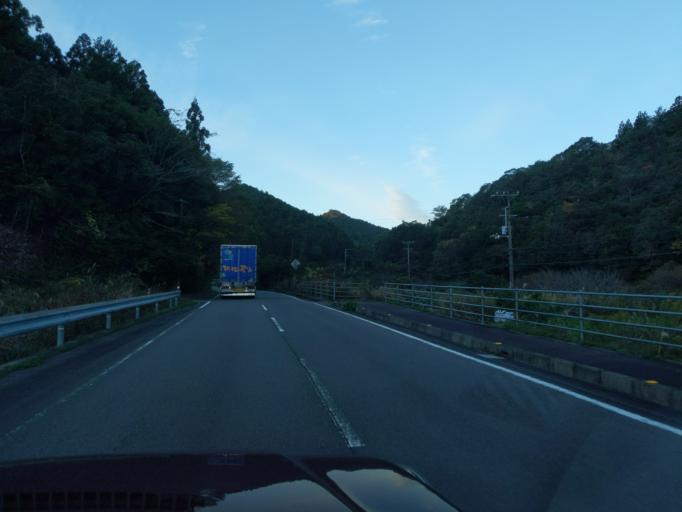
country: JP
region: Tokushima
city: Anan
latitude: 33.7101
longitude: 134.4708
